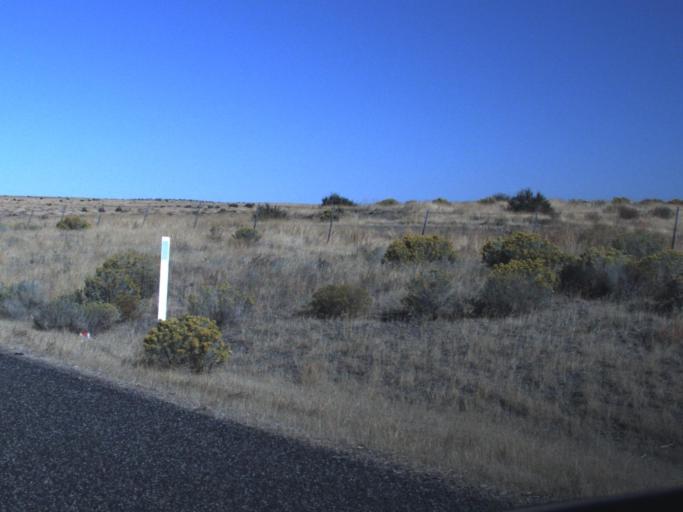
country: US
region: Washington
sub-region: Benton County
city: West Richland
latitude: 46.4100
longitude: -119.4522
